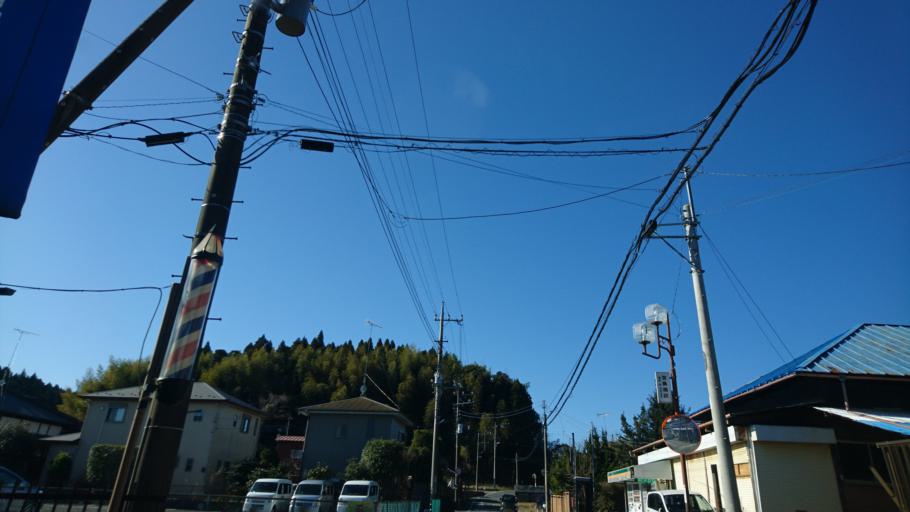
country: JP
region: Chiba
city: Yachimata
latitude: 35.6292
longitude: 140.3593
